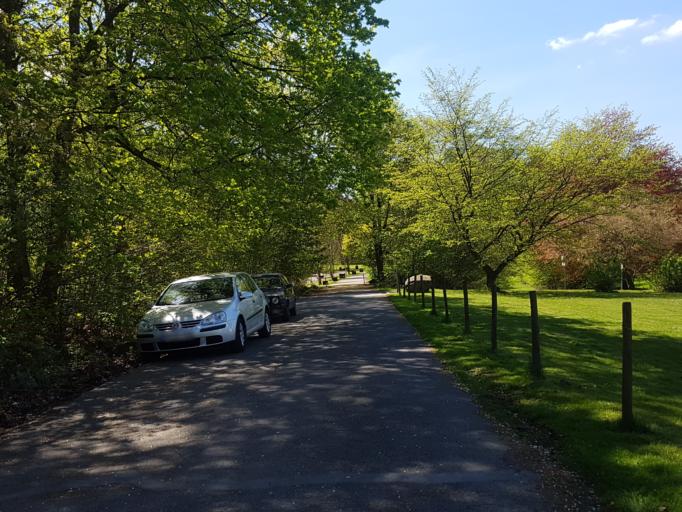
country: DE
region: North Rhine-Westphalia
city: Waldbrol
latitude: 50.8799
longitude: 7.6291
